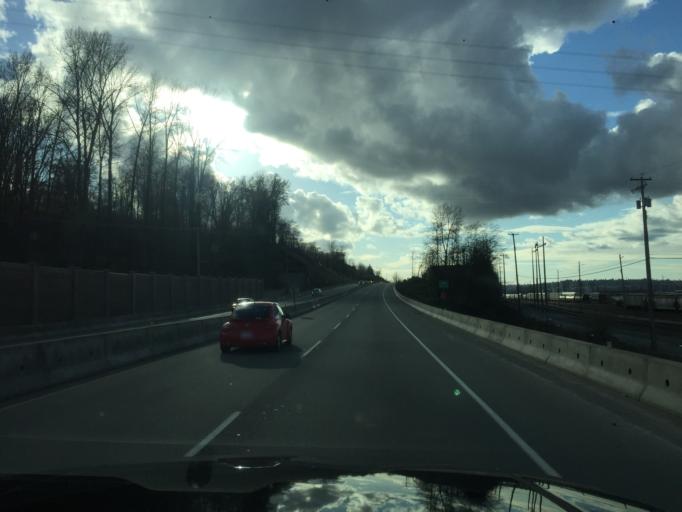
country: CA
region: British Columbia
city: Port Moody
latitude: 49.2146
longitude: -122.8218
